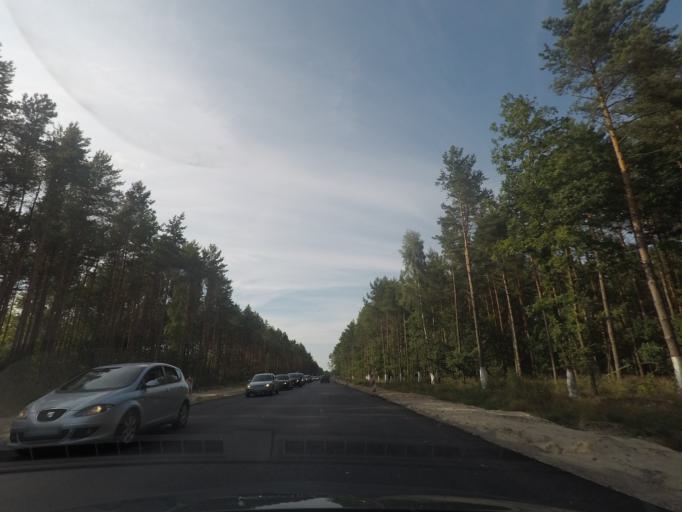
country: PL
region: Pomeranian Voivodeship
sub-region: Powiat leborski
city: Leba
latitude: 54.7154
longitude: 17.5767
